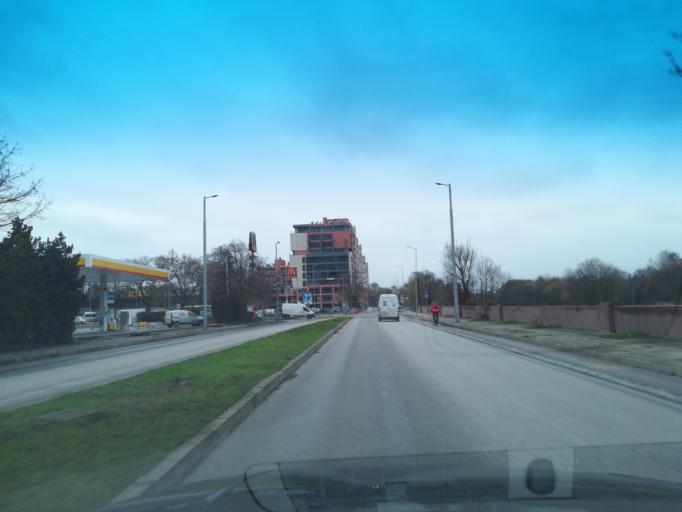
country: BG
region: Plovdiv
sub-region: Obshtina Plovdiv
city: Plovdiv
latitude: 42.1542
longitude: 24.7644
